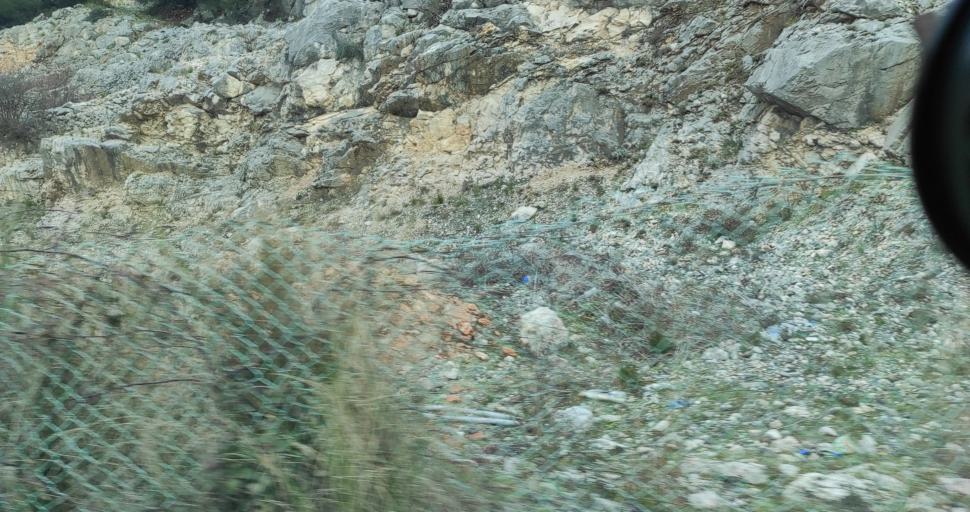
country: AL
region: Lezhe
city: Lezhe
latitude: 41.7884
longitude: 19.6269
